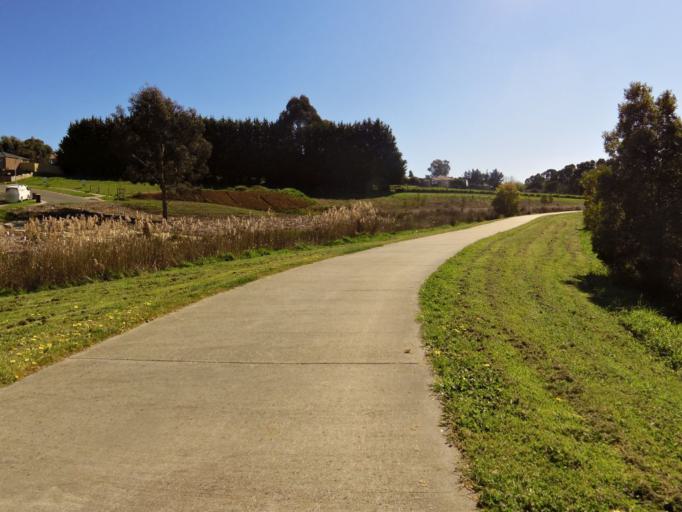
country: AU
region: Victoria
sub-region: Baw Baw
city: Warragul
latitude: -38.1290
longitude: 145.8706
